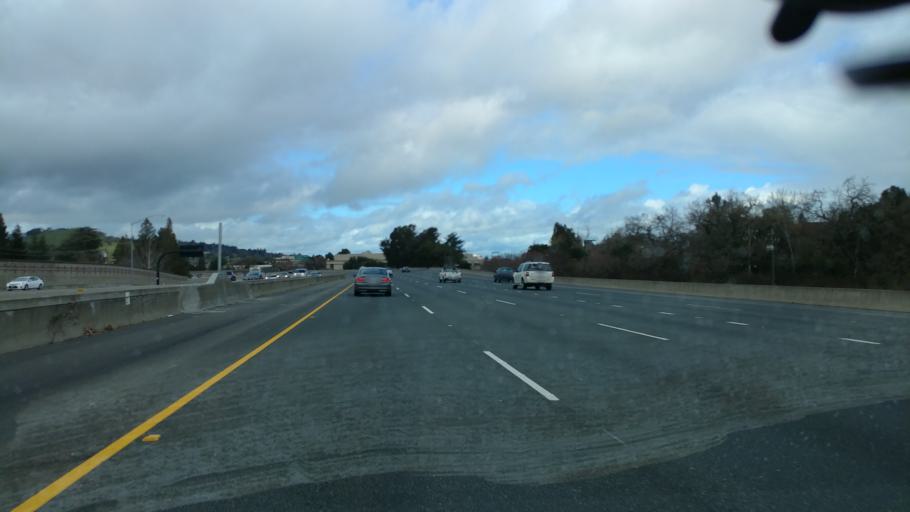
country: US
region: California
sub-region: Contra Costa County
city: Saranap
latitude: 37.8873
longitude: -122.0563
